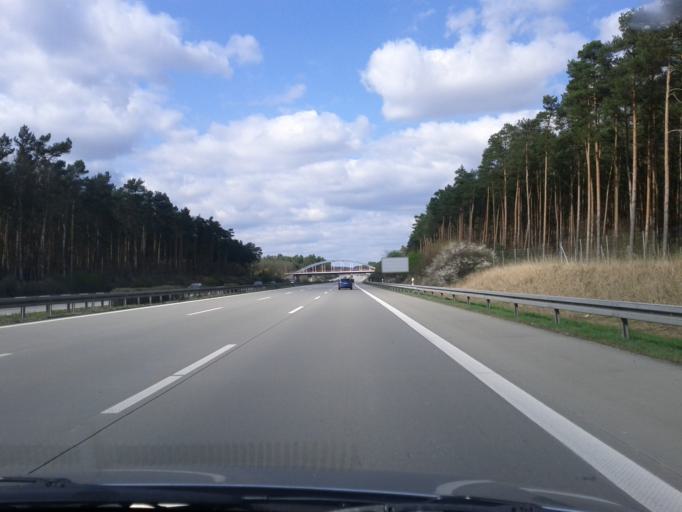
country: DE
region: Brandenburg
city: Grunheide
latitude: 52.4045
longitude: 13.7865
